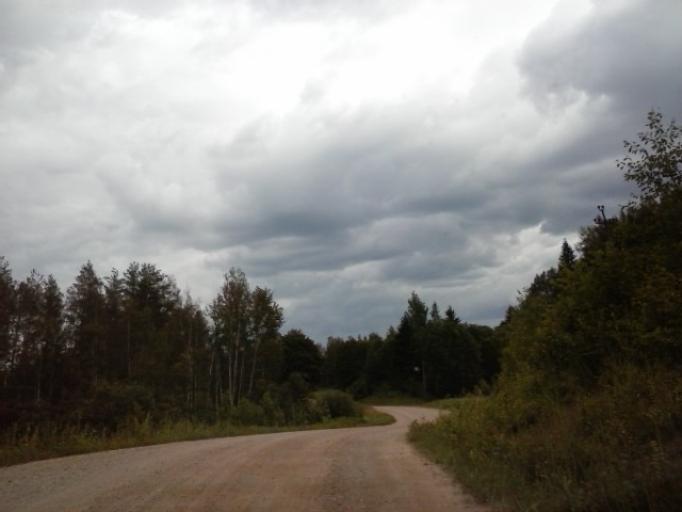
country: EE
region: Vorumaa
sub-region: Voru linn
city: Voru
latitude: 57.7416
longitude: 27.0932
